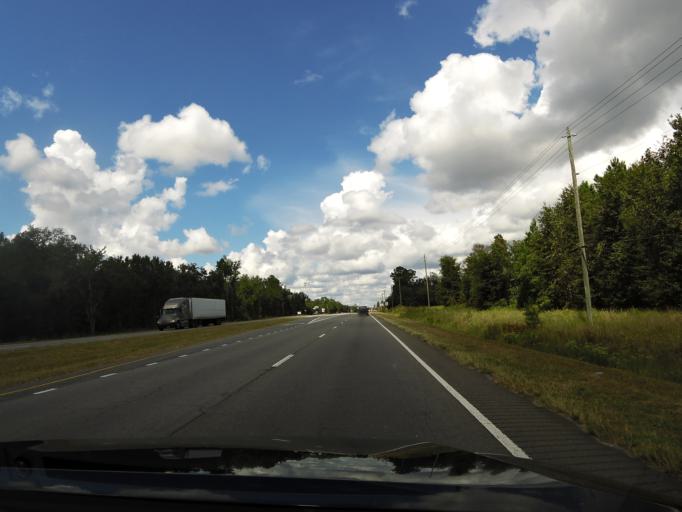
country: US
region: Georgia
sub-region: Charlton County
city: Folkston
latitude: 30.8173
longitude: -82.0004
